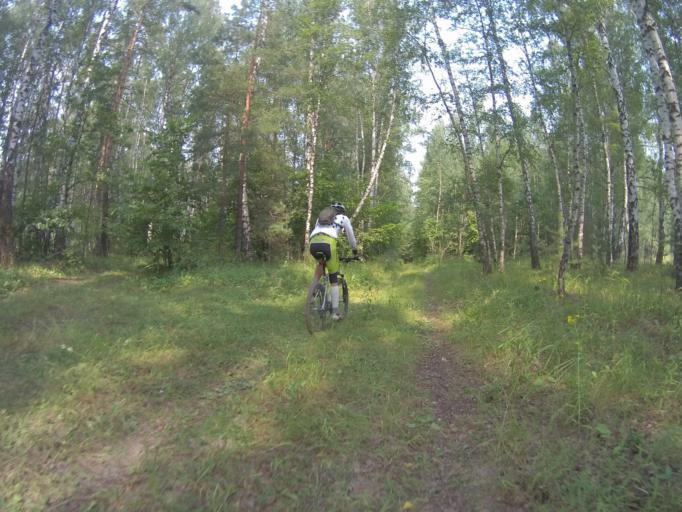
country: RU
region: Vladimir
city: Vorsha
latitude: 55.9834
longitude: 40.1917
